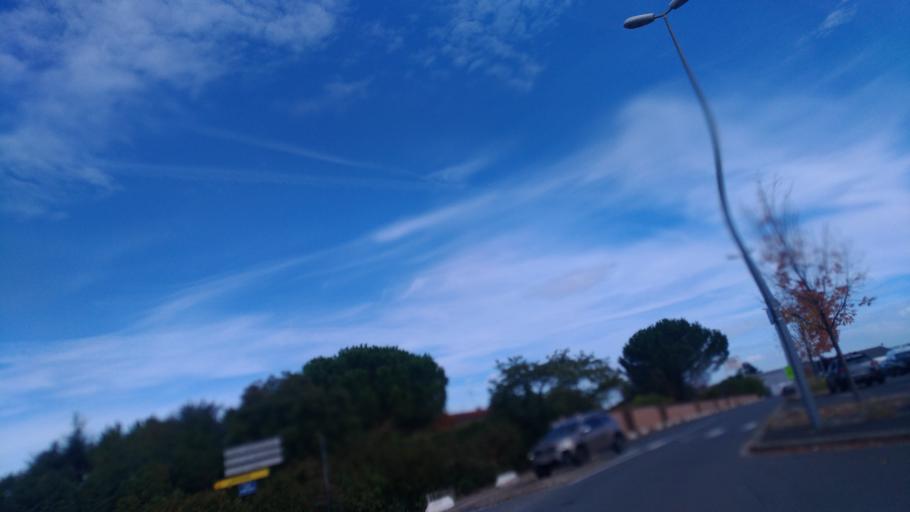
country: FR
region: Midi-Pyrenees
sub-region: Departement du Tarn
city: Puygouzon
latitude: 43.9197
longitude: 2.1655
